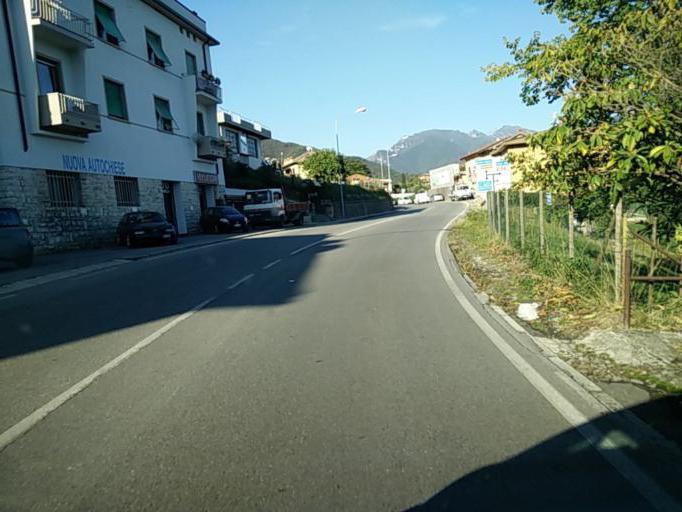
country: IT
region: Lombardy
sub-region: Provincia di Brescia
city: Roe Volciano
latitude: 45.6091
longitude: 10.4819
